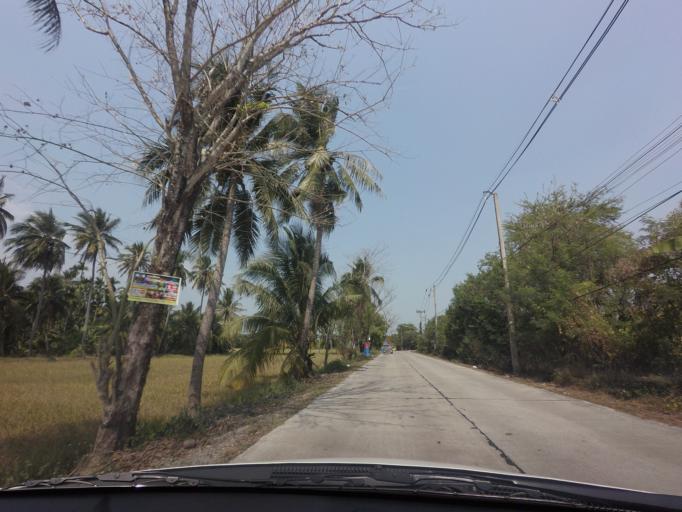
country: TH
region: Nakhon Pathom
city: Sam Phran
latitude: 13.7611
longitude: 100.2538
